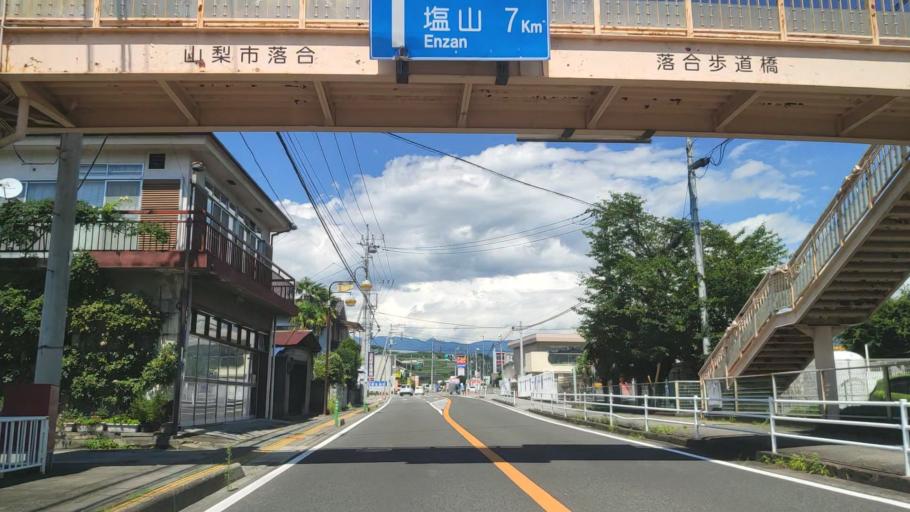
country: JP
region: Yamanashi
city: Isawa
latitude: 35.6850
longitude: 138.6659
